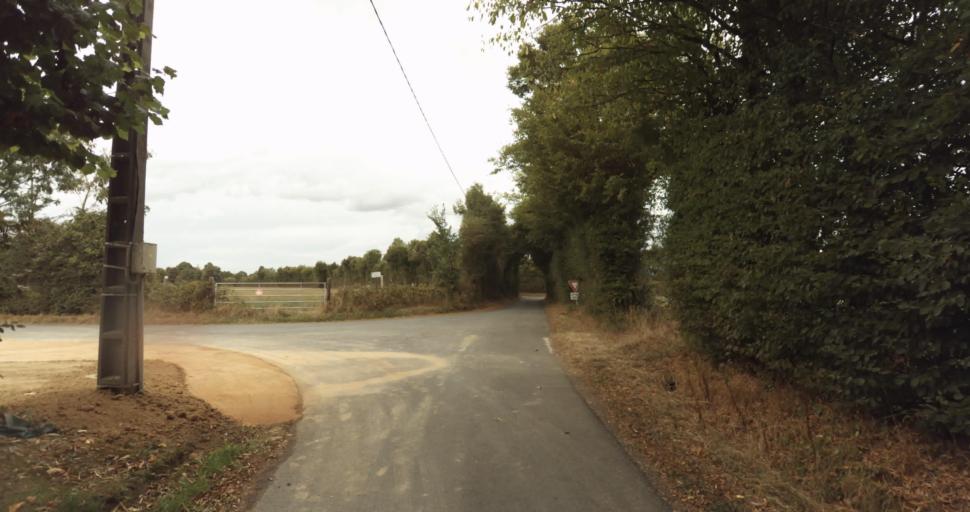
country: FR
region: Lower Normandy
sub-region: Departement de l'Orne
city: Gace
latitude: 48.8898
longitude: 0.3463
